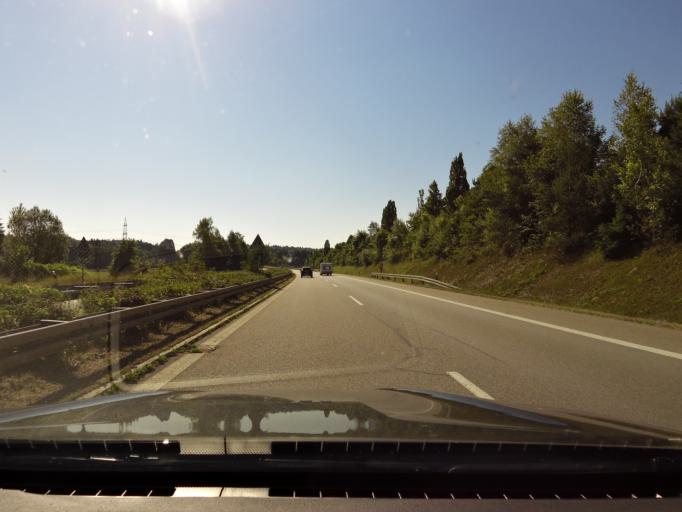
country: DE
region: Bavaria
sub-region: Upper Bavaria
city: Perach
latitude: 48.2495
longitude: 12.8038
